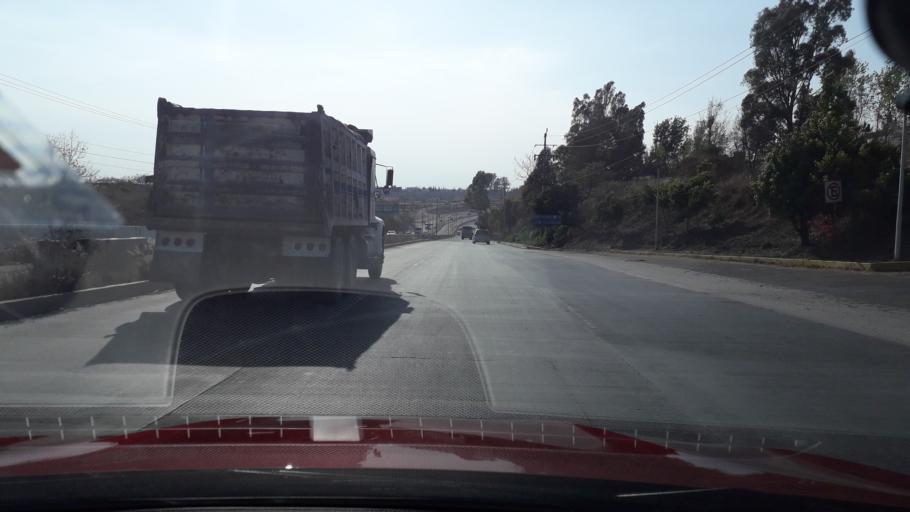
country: MX
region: Puebla
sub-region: Puebla
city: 18 de Marzo
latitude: 18.9720
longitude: -98.2041
